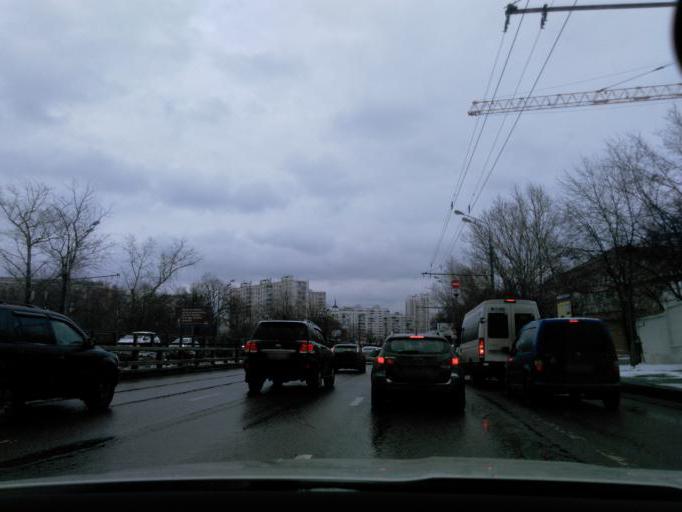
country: RU
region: Moscow
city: Likhobory
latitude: 55.8595
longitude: 37.5559
